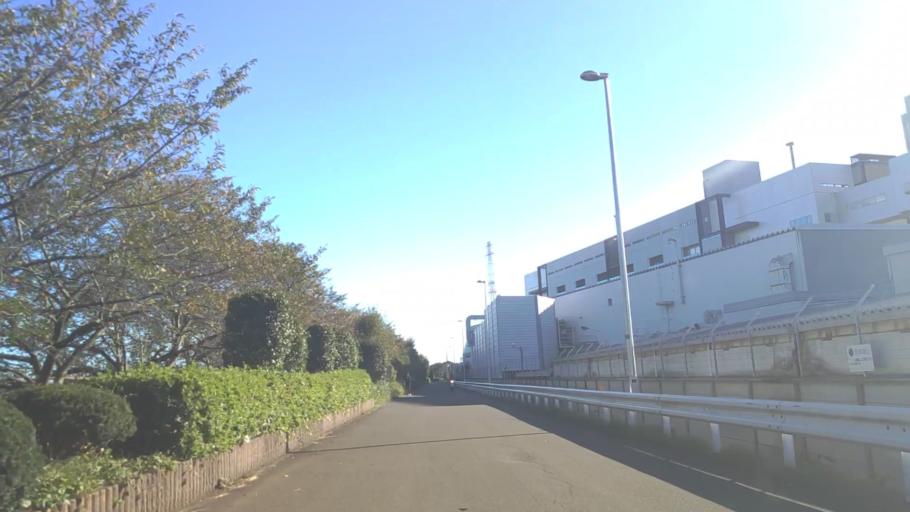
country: JP
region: Kanagawa
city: Atsugi
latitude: 35.4342
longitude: 139.3713
